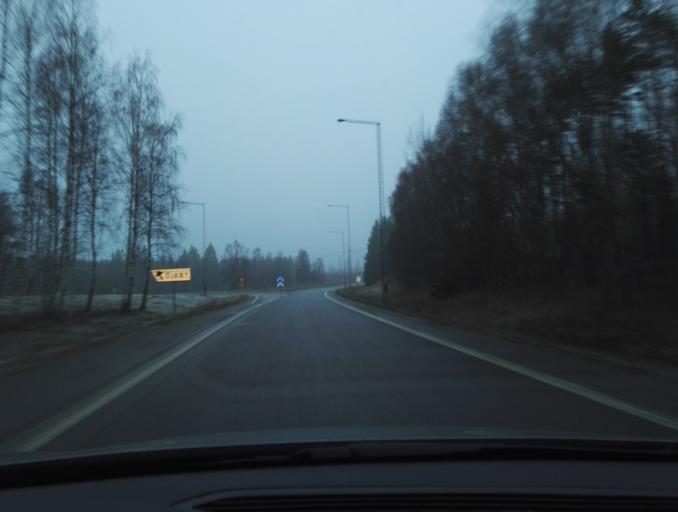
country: SE
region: Kronoberg
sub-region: Vaxjo Kommun
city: Vaexjoe
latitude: 56.8971
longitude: 14.7315
